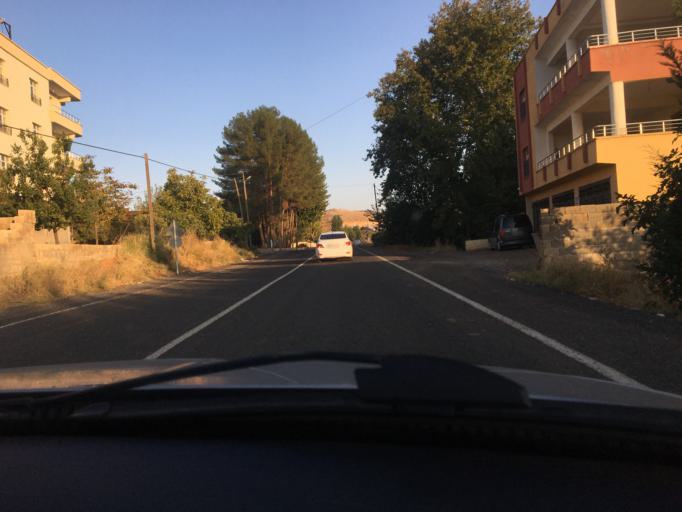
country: TR
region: Sanliurfa
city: Halfeti
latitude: 37.2087
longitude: 37.9662
